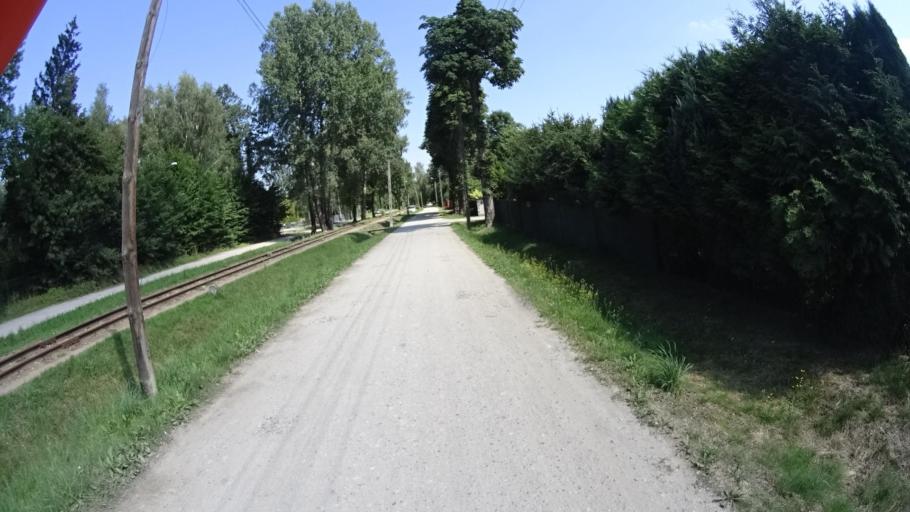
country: PL
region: Masovian Voivodeship
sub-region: Powiat piaseczynski
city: Prazmow
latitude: 52.0058
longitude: 20.9133
